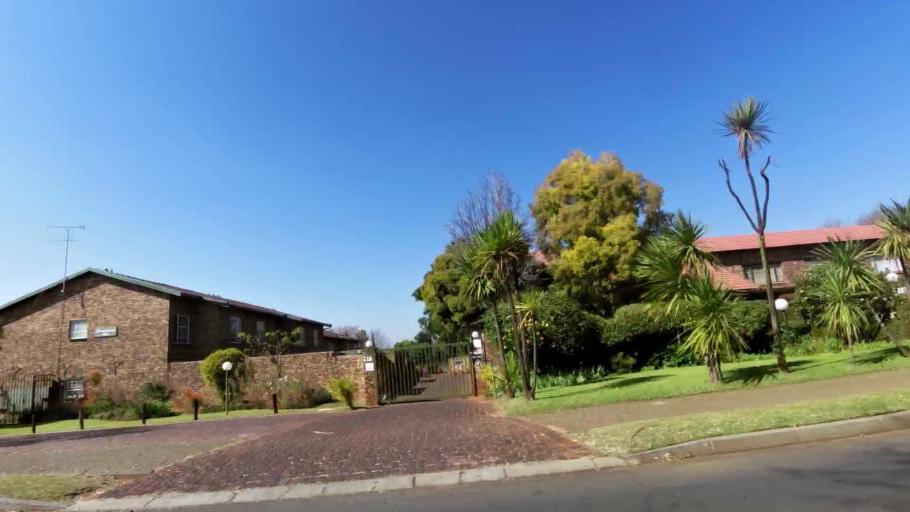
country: ZA
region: Gauteng
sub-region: City of Johannesburg Metropolitan Municipality
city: Roodepoort
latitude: -26.1273
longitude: 27.9469
